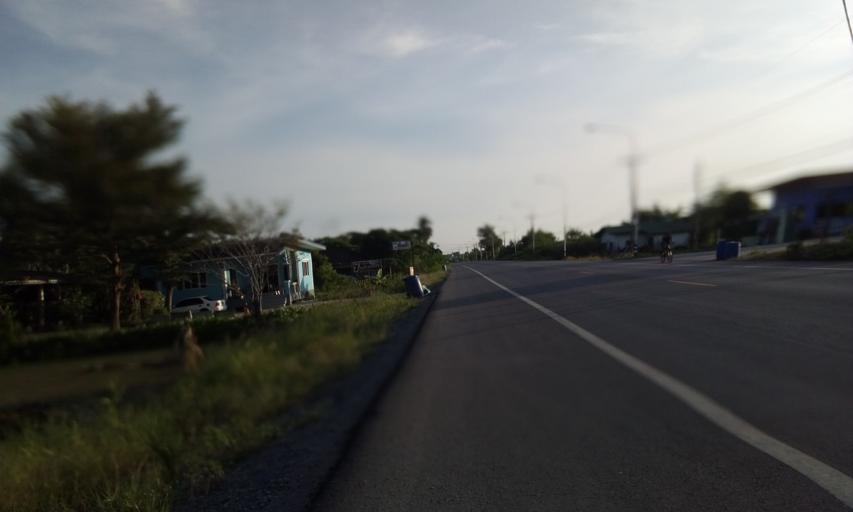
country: TH
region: Pathum Thani
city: Ban Rangsit
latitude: 14.0409
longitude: 100.8443
